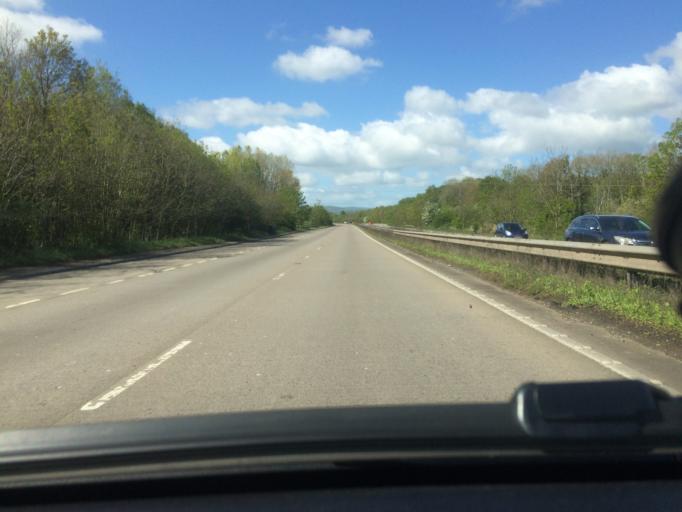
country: GB
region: Wales
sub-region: Wrexham
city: Rossett
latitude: 53.1471
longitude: -2.9277
